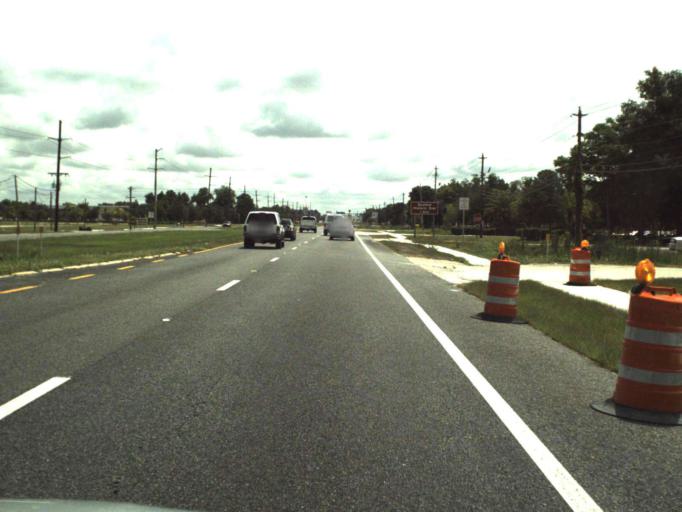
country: US
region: Florida
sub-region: Seminole County
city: Sanford
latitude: 28.8112
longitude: -81.3081
